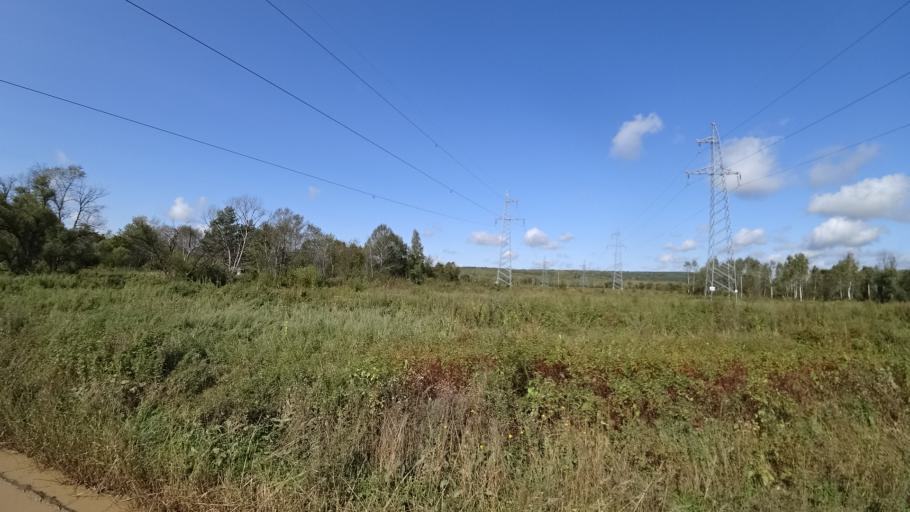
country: RU
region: Amur
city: Arkhara
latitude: 49.4091
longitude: 130.1617
